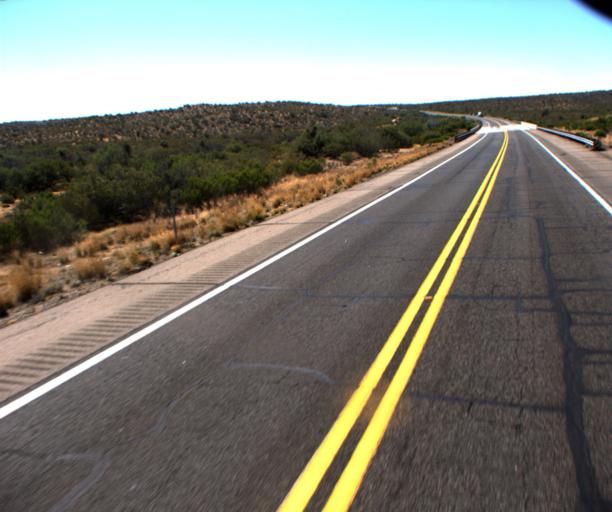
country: US
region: Arizona
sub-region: Yavapai County
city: Congress
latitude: 34.2072
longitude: -113.0646
